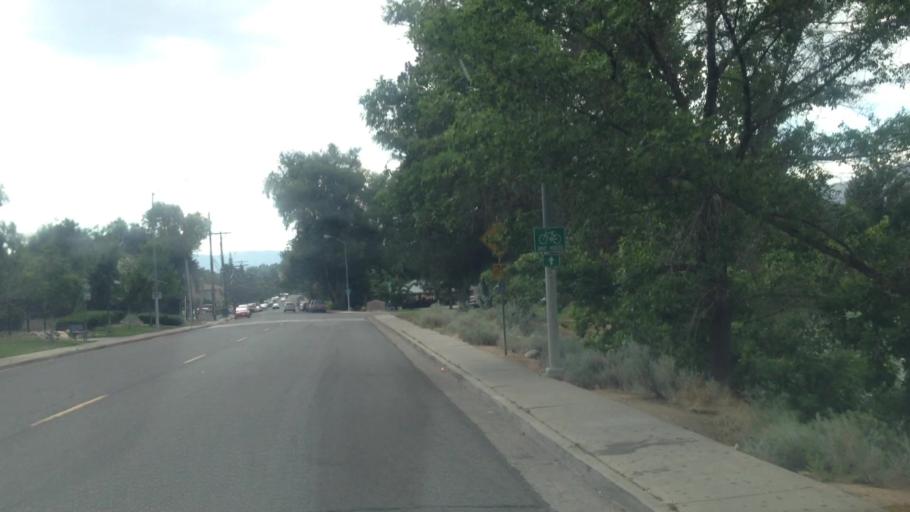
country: US
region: Nevada
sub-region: Washoe County
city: Reno
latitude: 39.5199
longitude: -119.8300
